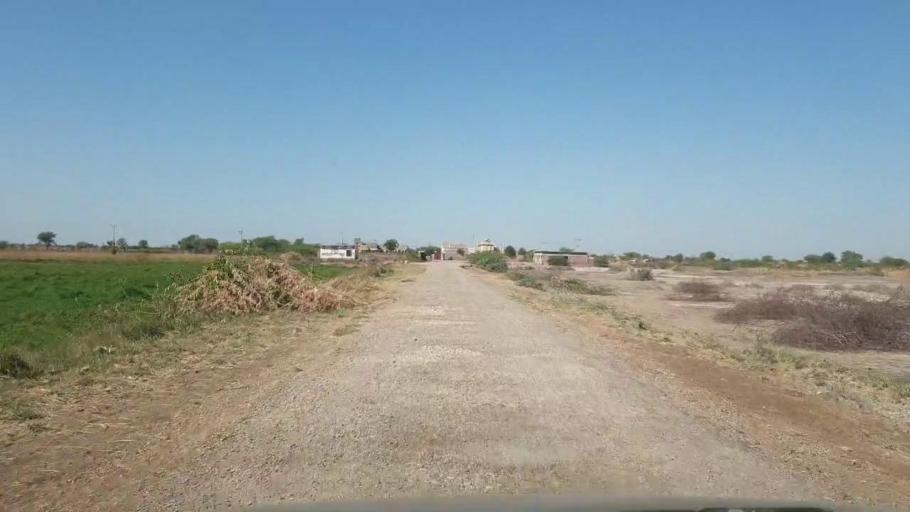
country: PK
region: Sindh
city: Dhoro Naro
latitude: 25.4018
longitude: 69.6184
